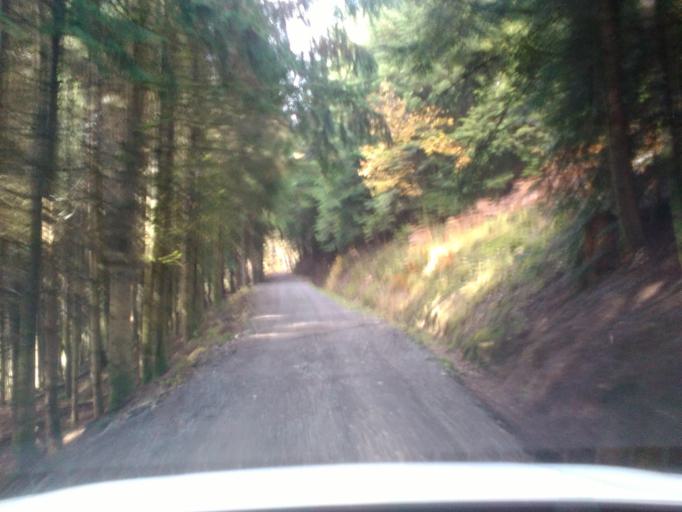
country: FR
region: Lorraine
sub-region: Departement des Vosges
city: Senones
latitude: 48.4144
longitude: 6.9808
